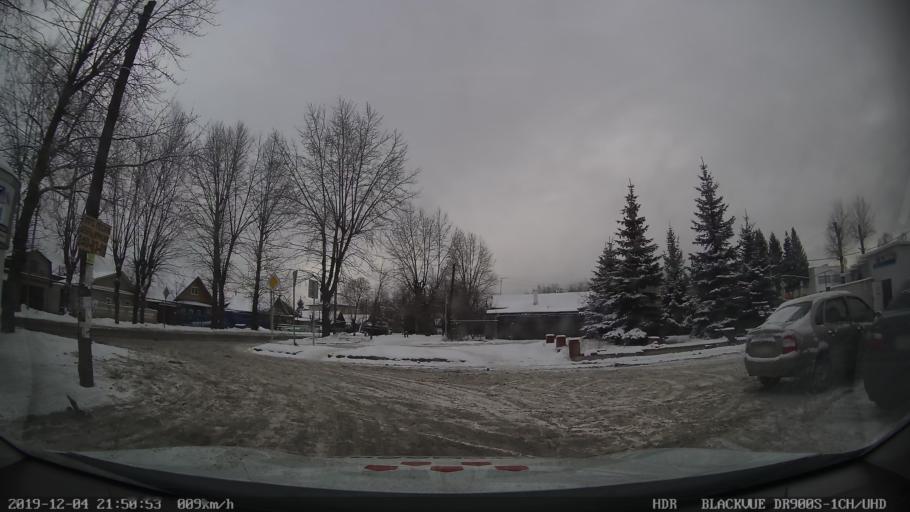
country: RU
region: Tatarstan
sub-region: Gorod Kazan'
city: Kazan
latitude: 55.7089
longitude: 49.1464
